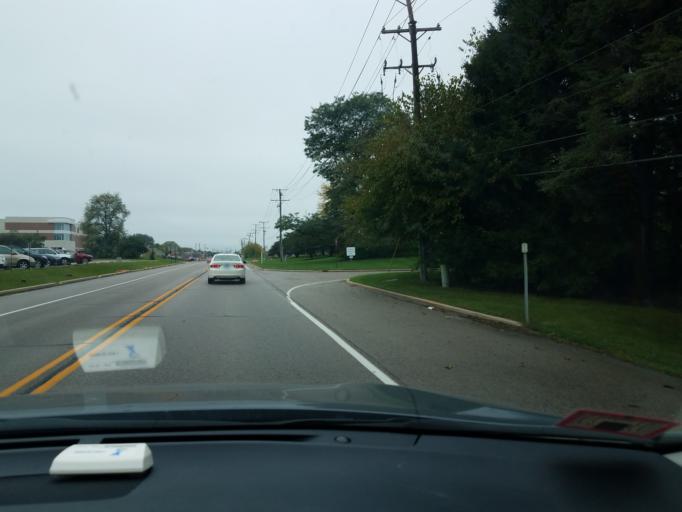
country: US
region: Illinois
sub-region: Lake County
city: Riverwoods
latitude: 42.1677
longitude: -87.9171
